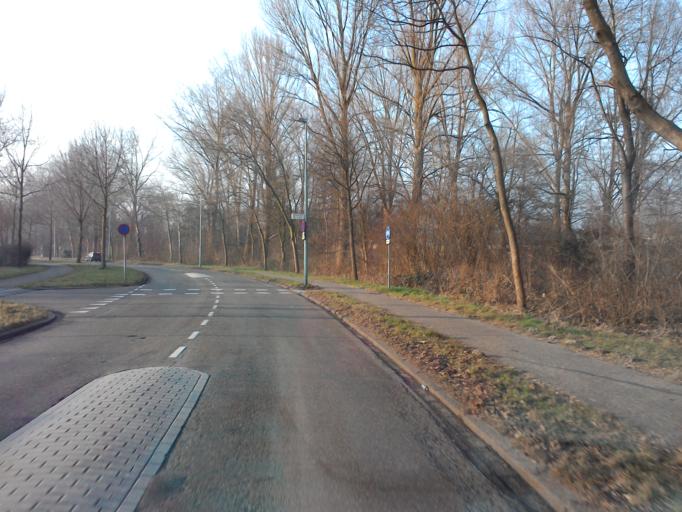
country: NL
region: Utrecht
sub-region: Gemeente Zeist
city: Zeist
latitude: 52.0847
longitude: 5.2131
